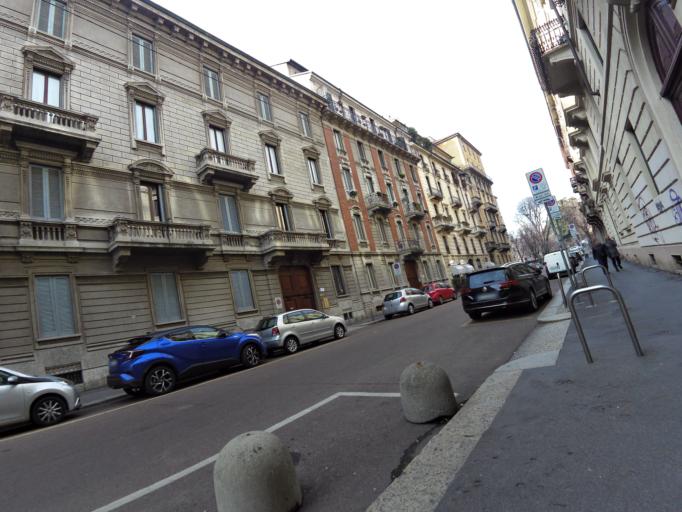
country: IT
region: Lombardy
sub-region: Citta metropolitana di Milano
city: Milano
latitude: 45.4688
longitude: 9.1737
